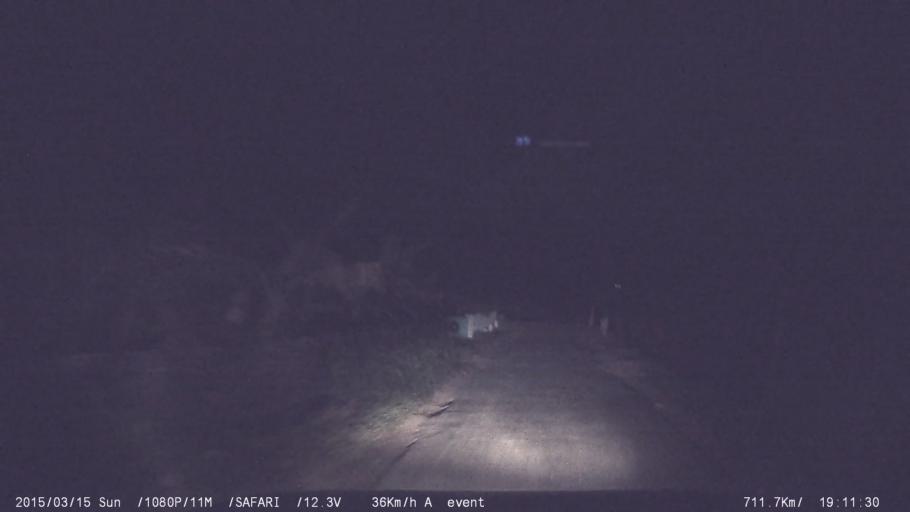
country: IN
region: Kerala
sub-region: Ernakulam
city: Piravam
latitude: 9.8713
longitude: 76.6135
